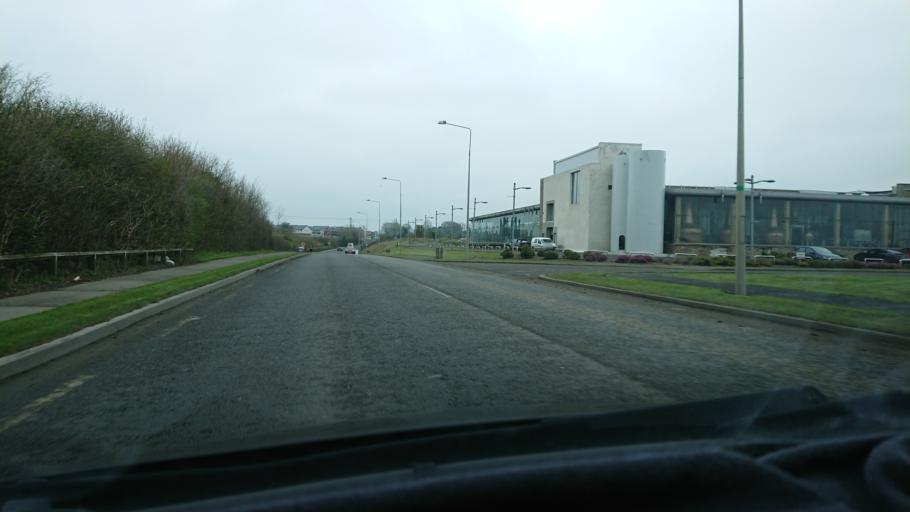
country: IE
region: Leinster
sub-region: Lu
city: Drogheda
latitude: 53.6944
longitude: -6.3691
